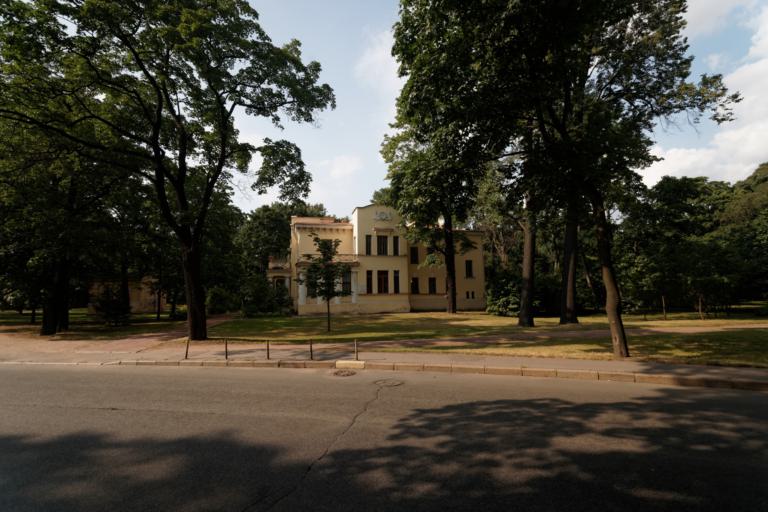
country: RU
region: St.-Petersburg
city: Novaya Derevnya
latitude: 59.9768
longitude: 30.2940
